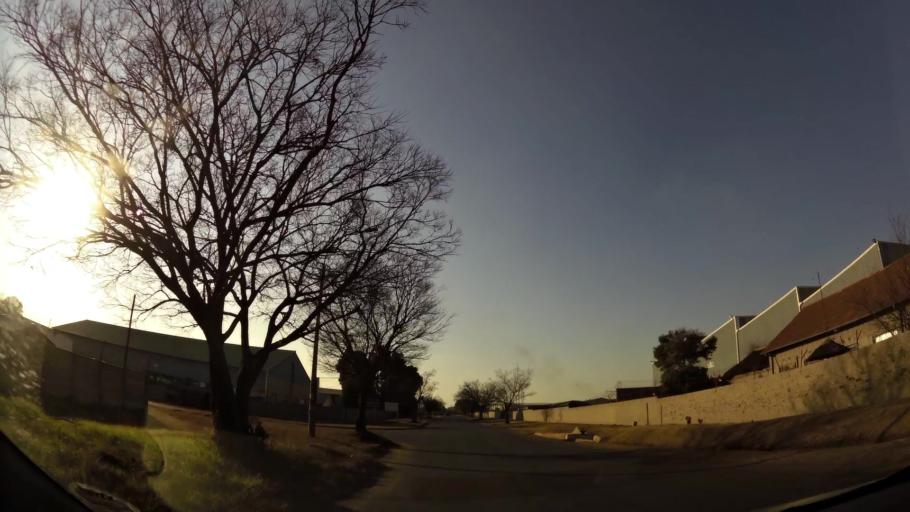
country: ZA
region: Gauteng
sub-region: West Rand District Municipality
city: Randfontein
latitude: -26.2009
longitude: 27.6835
